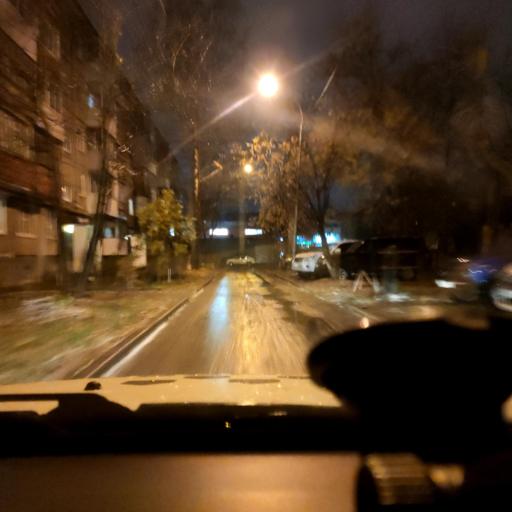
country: RU
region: Perm
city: Perm
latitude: 57.9648
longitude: 56.2273
